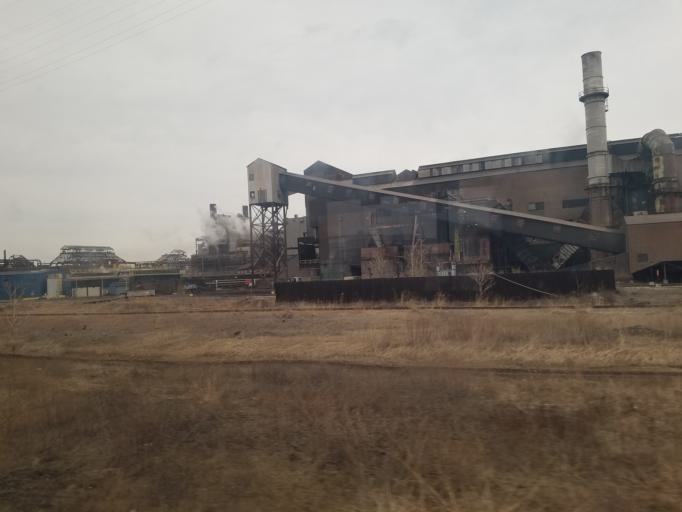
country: US
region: Indiana
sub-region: Lake County
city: East Chicago
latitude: 41.6609
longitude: -87.4533
